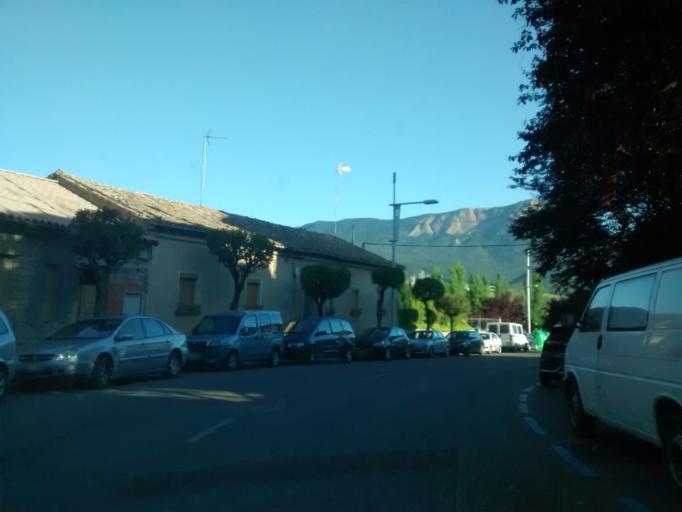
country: ES
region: Aragon
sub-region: Provincia de Huesca
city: Jaca
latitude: 42.5702
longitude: -0.5463
